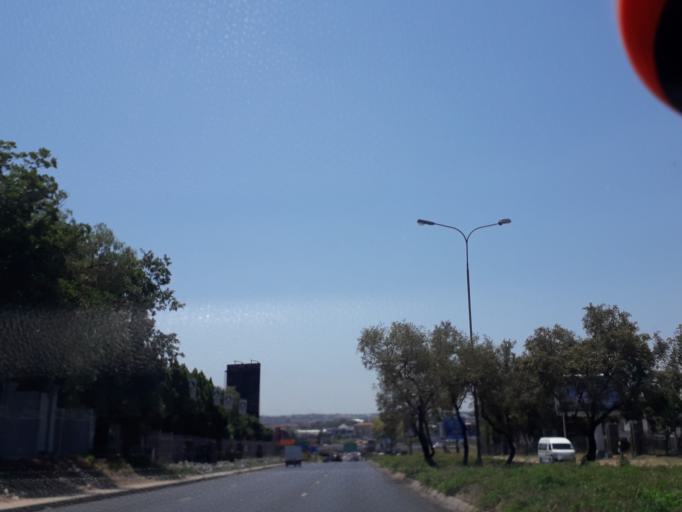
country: ZA
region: Gauteng
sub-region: City of Johannesburg Metropolitan Municipality
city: Midrand
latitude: -26.0424
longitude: 28.0601
